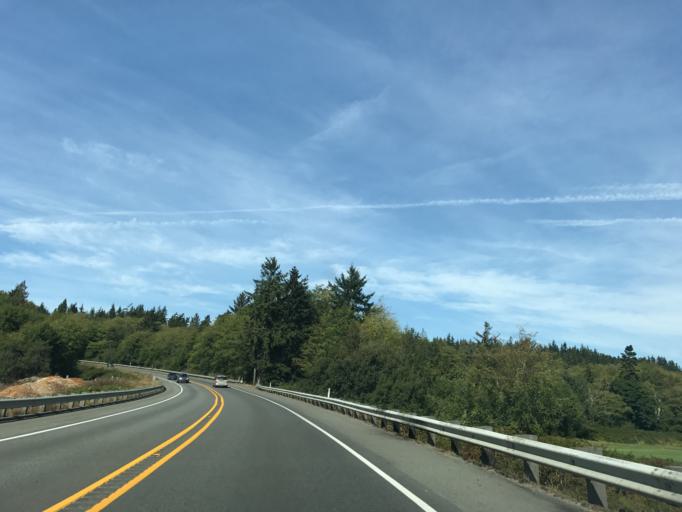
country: US
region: Washington
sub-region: Island County
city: Ault Field
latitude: 48.3542
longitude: -122.6123
